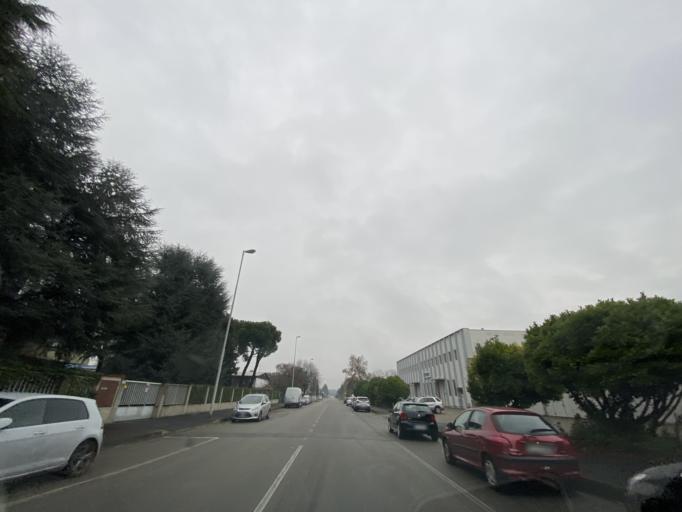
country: IT
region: Lombardy
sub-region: Citta metropolitana di Milano
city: Cusago
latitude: 45.4439
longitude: 9.0453
